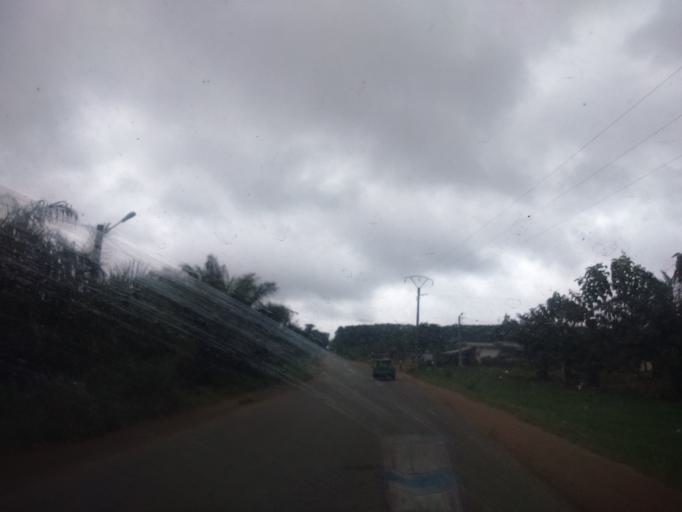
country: CI
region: Sud-Comoe
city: Bonoua
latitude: 5.2772
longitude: -3.5051
